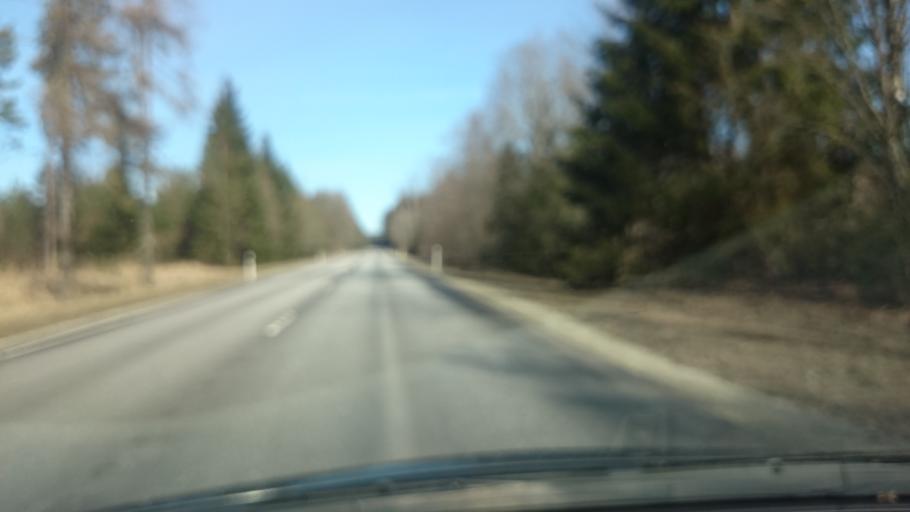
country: EE
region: Jaervamaa
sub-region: Tueri vald
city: Sarevere
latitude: 58.6902
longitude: 25.2465
